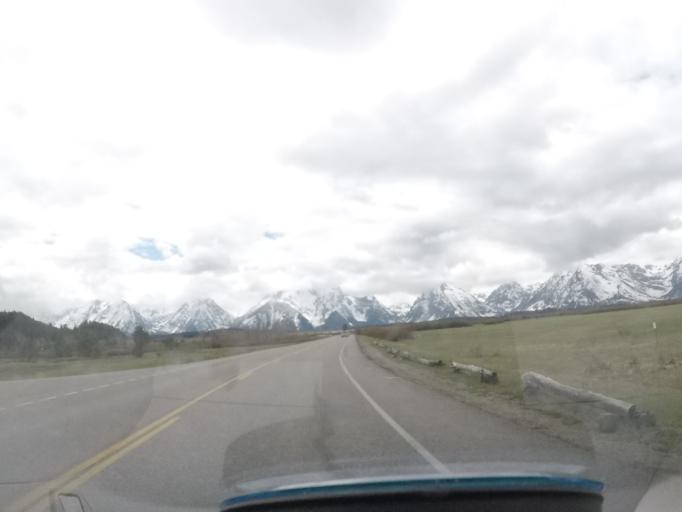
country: US
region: Wyoming
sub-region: Teton County
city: Jackson
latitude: 43.8624
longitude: -110.5762
